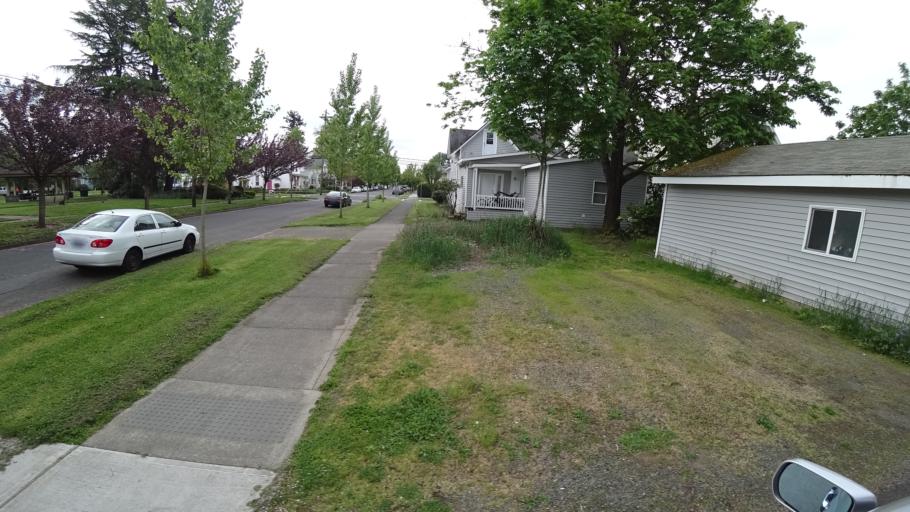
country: US
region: Oregon
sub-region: Washington County
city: Hillsboro
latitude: 45.5257
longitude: -122.9880
